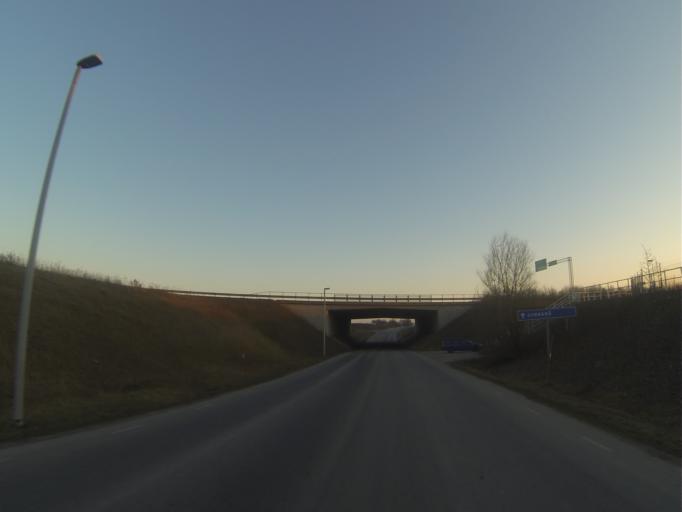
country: SE
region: Skane
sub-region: Burlovs Kommun
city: Arloev
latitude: 55.6168
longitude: 13.1225
